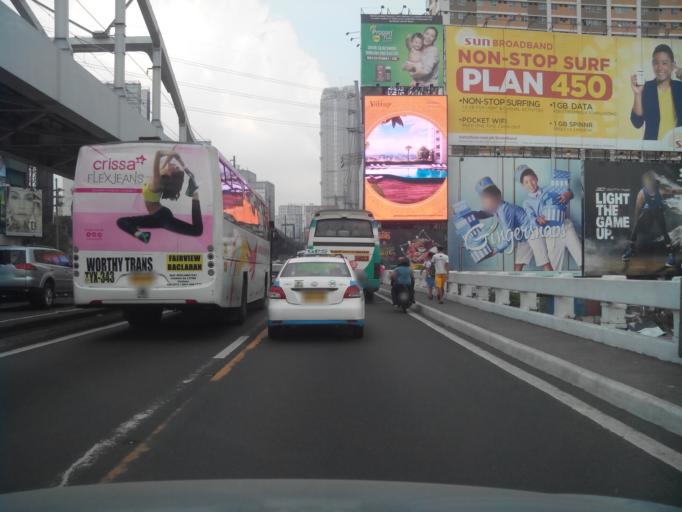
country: PH
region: Metro Manila
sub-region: Mandaluyong
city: Mandaluyong City
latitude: 14.5683
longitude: 121.0461
